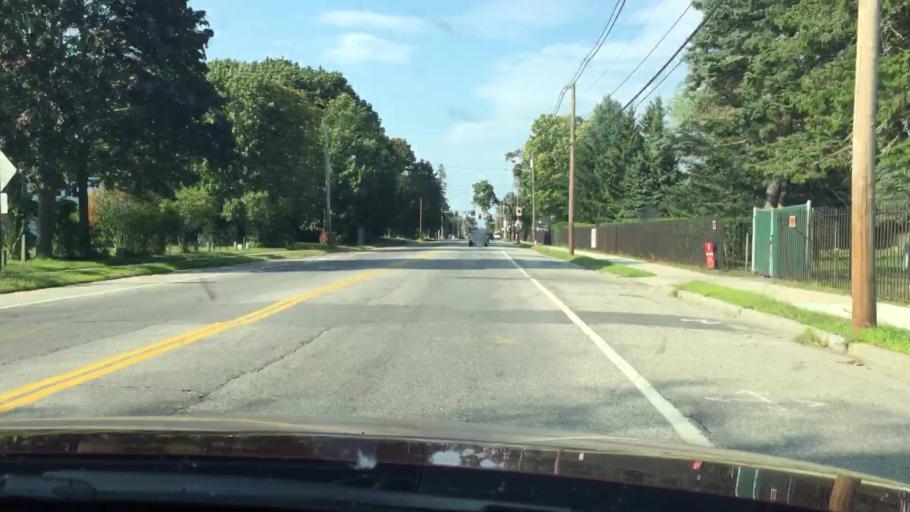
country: US
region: Maine
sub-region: Cumberland County
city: Portland
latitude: 43.6787
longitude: -70.2944
